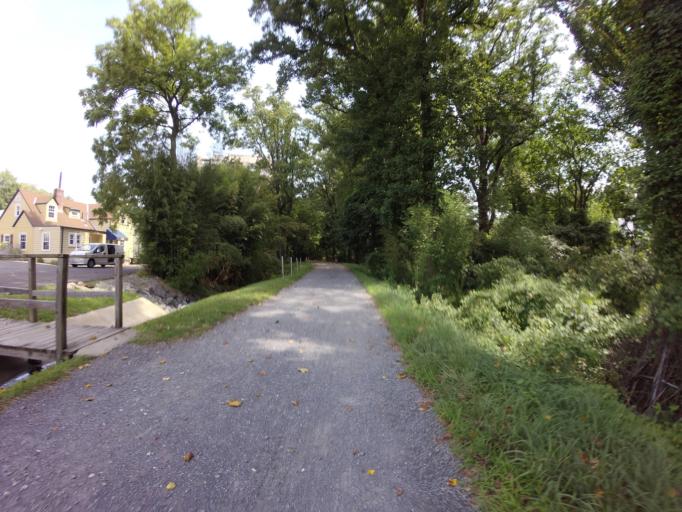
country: US
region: Maryland
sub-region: Montgomery County
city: Bethesda
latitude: 38.9846
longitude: -77.0870
